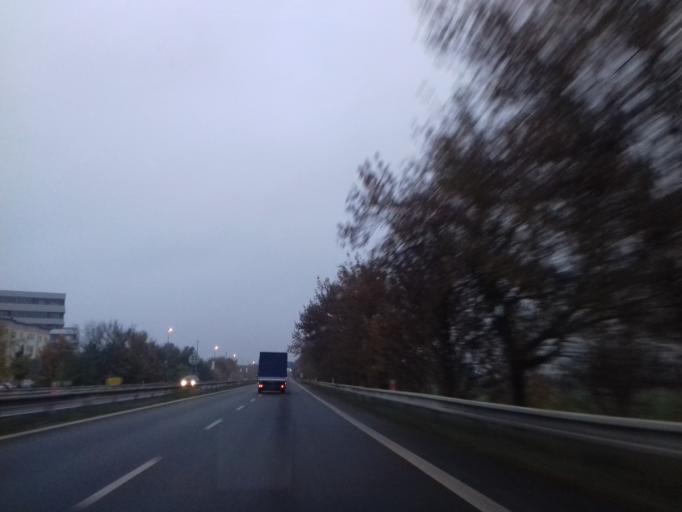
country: CZ
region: Olomoucky
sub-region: Okres Olomouc
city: Olomouc
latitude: 49.6000
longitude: 17.2298
